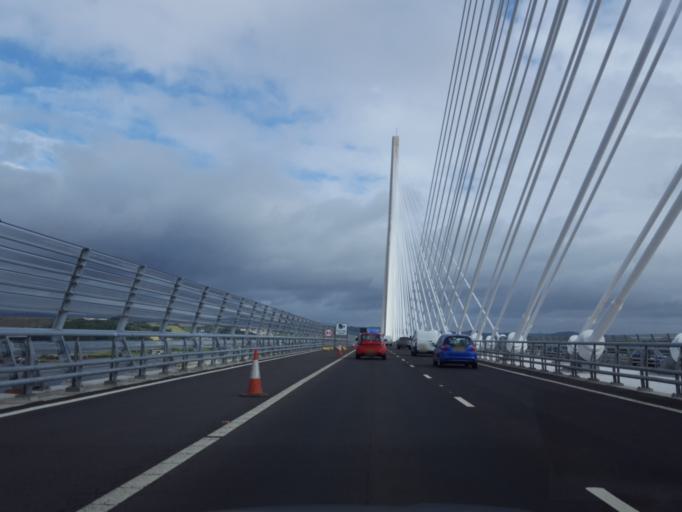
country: GB
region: Scotland
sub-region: Edinburgh
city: Queensferry
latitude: 56.0059
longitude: -3.4117
